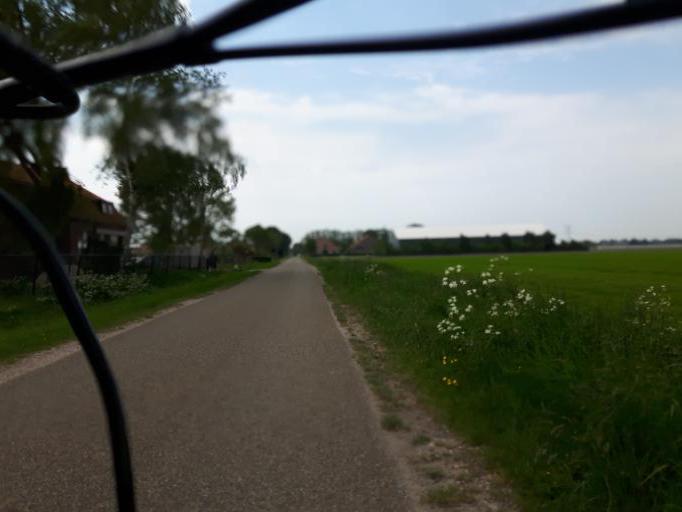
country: NL
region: North Brabant
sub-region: Gemeente Steenbergen
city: Welberg
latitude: 51.5390
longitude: 4.3506
